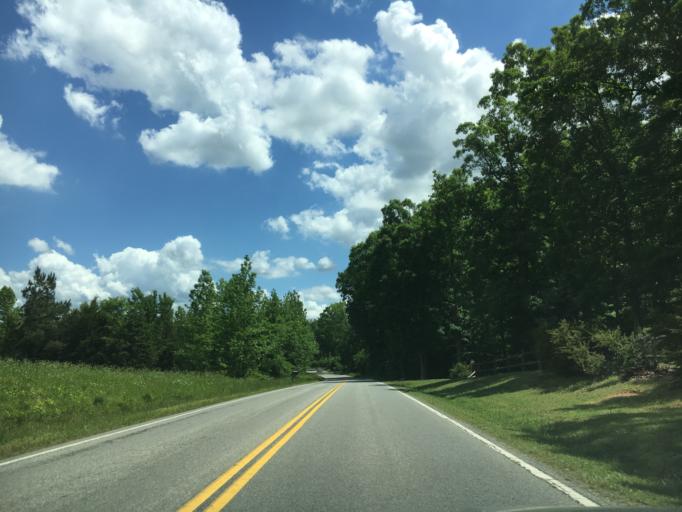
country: US
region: Virginia
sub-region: Halifax County
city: South Boston
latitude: 36.7168
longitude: -78.9400
